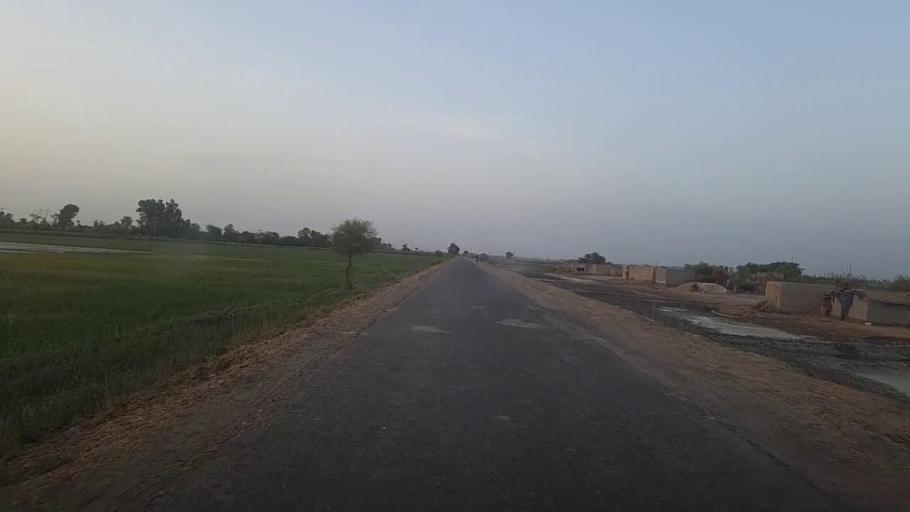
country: PK
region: Sindh
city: Radhan
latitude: 27.1383
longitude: 67.9334
